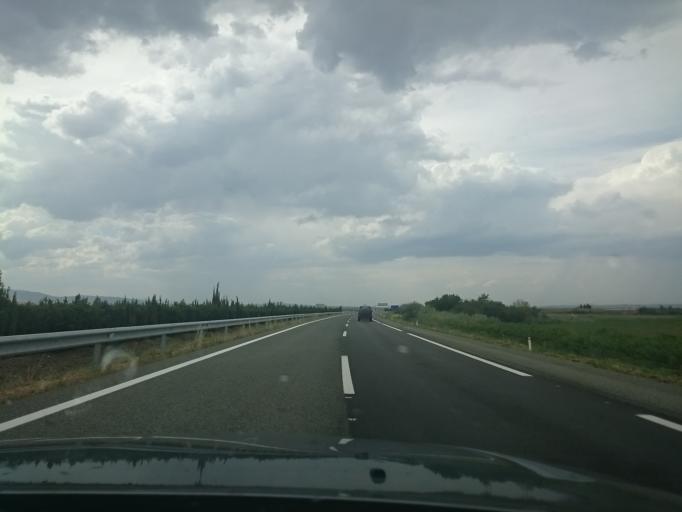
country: ES
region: Navarre
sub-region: Provincia de Navarra
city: Corella
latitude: 42.1385
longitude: -1.7782
